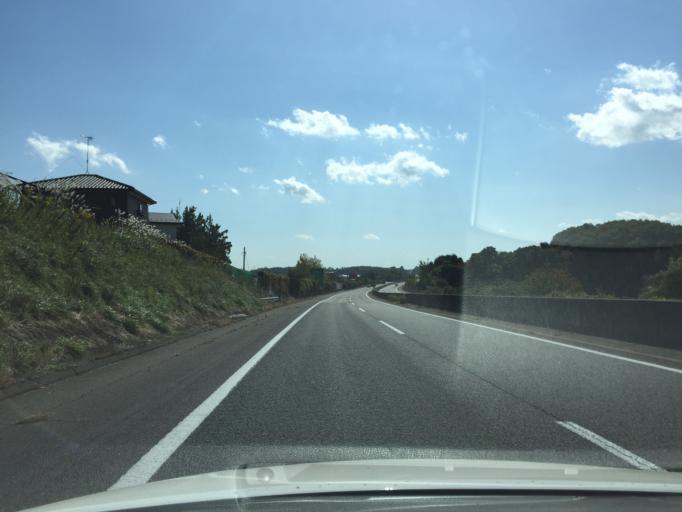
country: JP
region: Fukushima
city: Sukagawa
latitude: 37.2973
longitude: 140.3516
